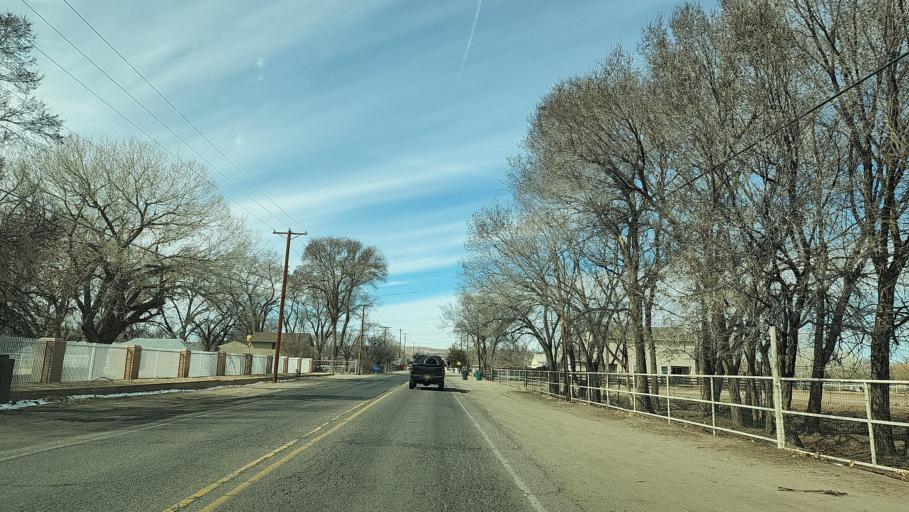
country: US
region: New Mexico
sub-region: Bernalillo County
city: South Valley
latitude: 35.0360
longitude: -106.7055
